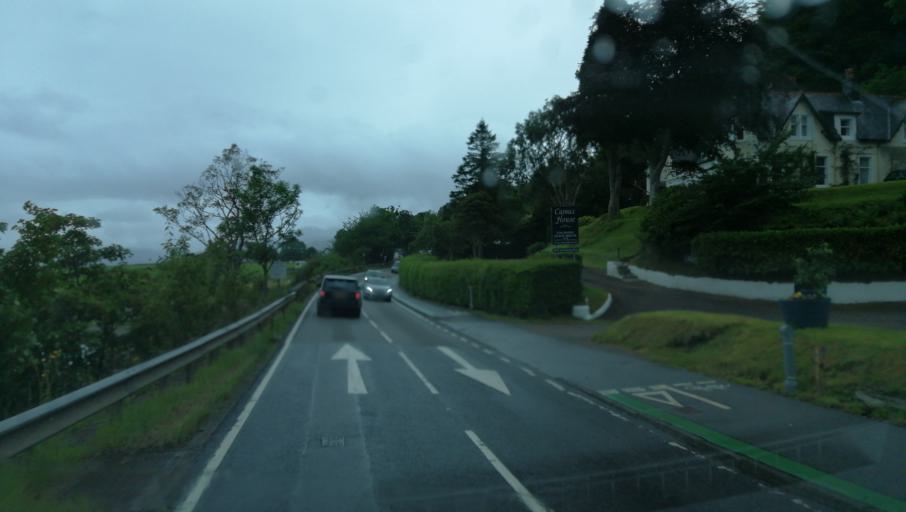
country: GB
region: Scotland
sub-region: Highland
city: Fort William
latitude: 56.7027
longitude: -5.2179
